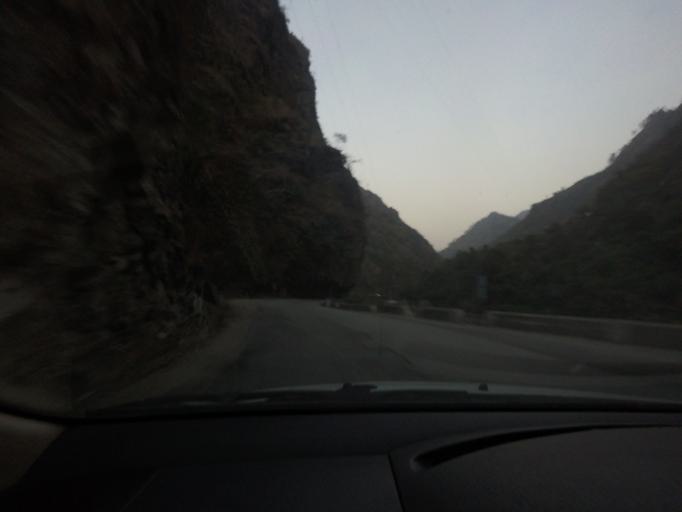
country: IN
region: Himachal Pradesh
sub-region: Mandi
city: Pandoh
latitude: 31.6948
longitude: 77.1487
